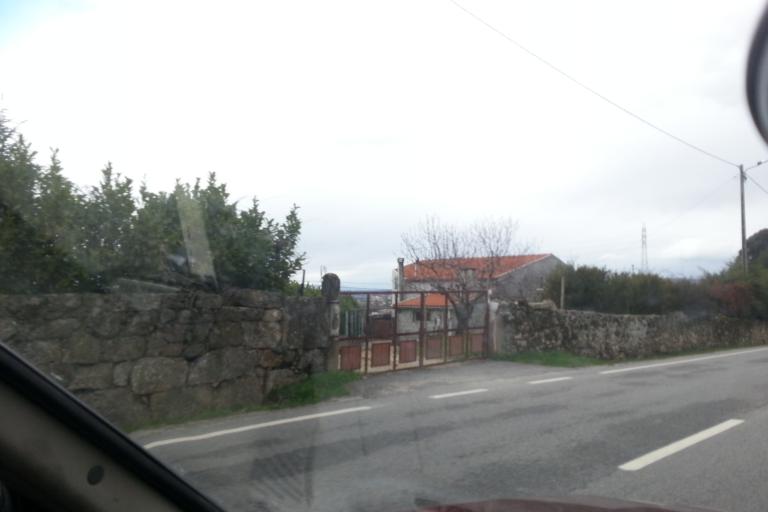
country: PT
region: Guarda
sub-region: Manteigas
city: Manteigas
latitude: 40.5077
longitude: -7.5886
